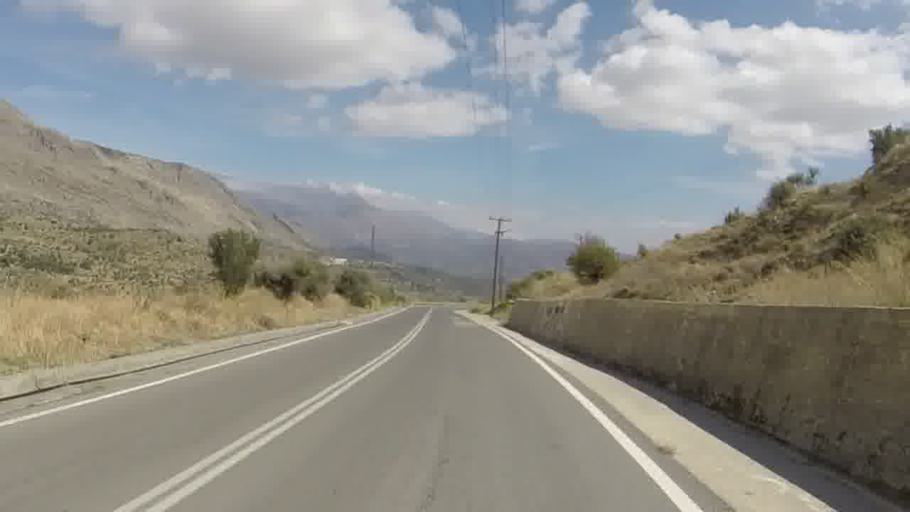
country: GR
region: Crete
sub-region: Nomos Rethymnis
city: Agia Galini
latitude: 35.1423
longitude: 24.6358
